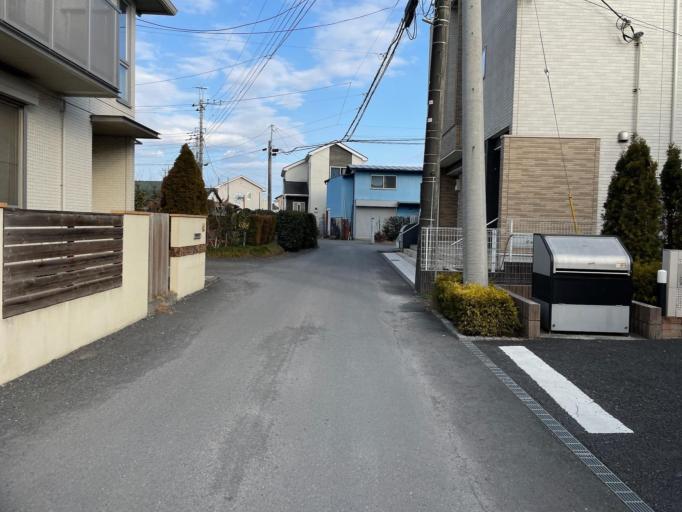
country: JP
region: Saitama
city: Hanno
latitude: 35.8388
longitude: 139.3416
